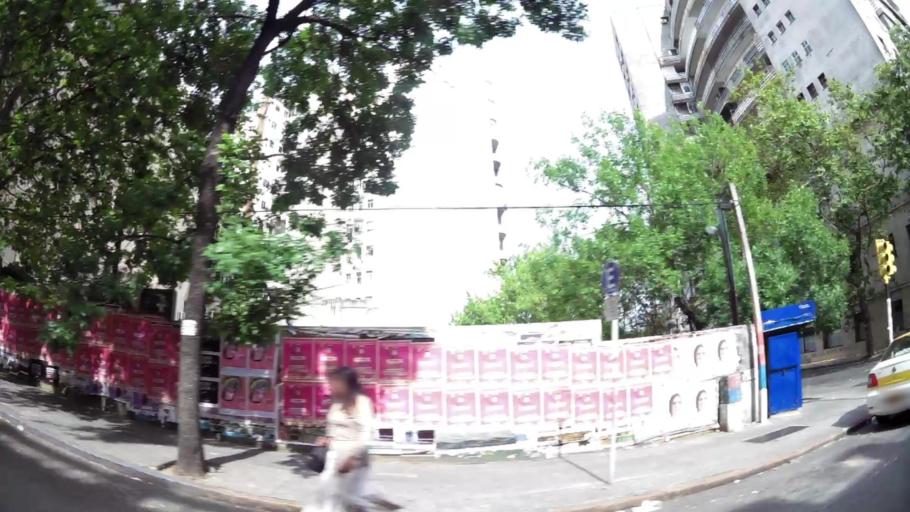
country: UY
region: Montevideo
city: Montevideo
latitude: -34.9042
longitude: -56.1927
